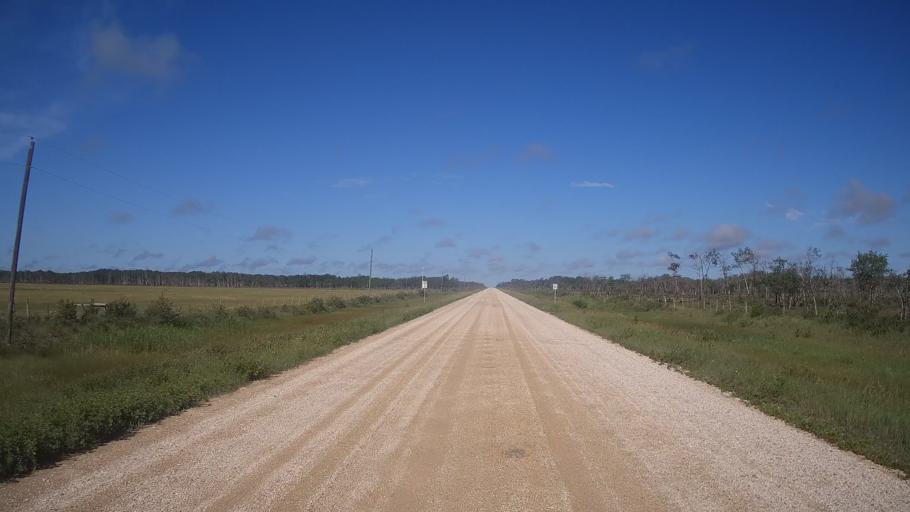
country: CA
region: Manitoba
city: Stonewall
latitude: 50.2410
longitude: -97.7403
